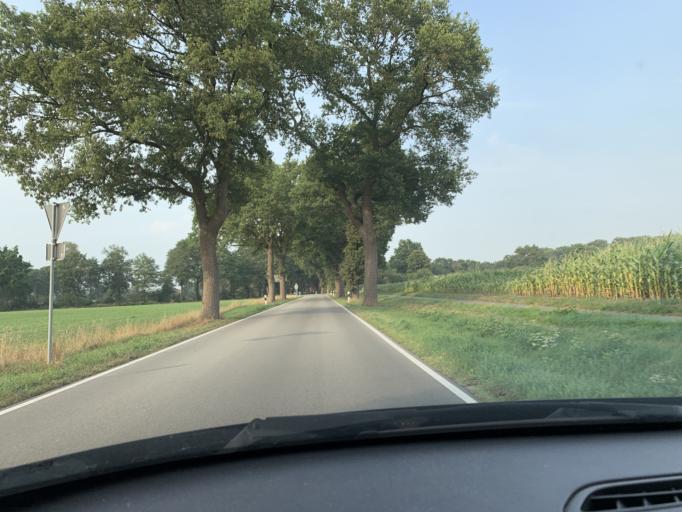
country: DE
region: Lower Saxony
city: Apen
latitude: 53.1800
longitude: 7.7802
